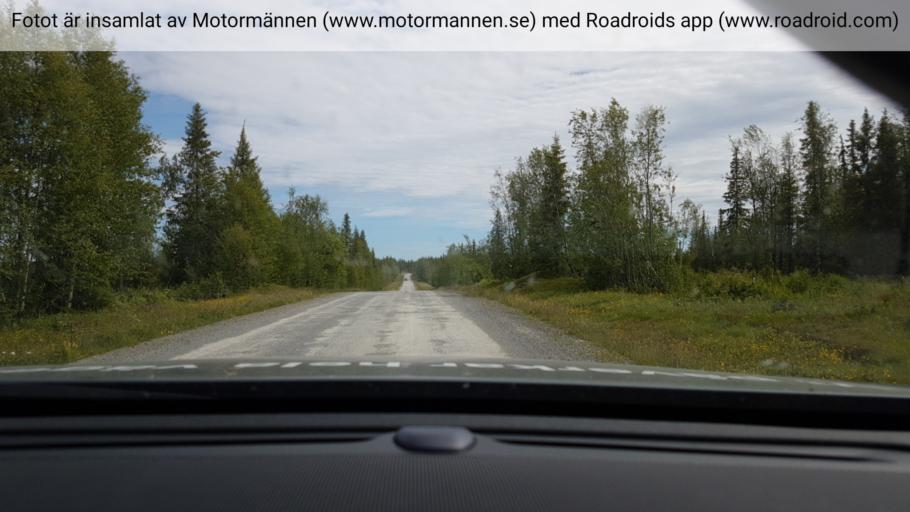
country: SE
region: Vaesterbotten
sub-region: Vilhelmina Kommun
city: Sjoberg
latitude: 65.1921
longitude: 16.1856
